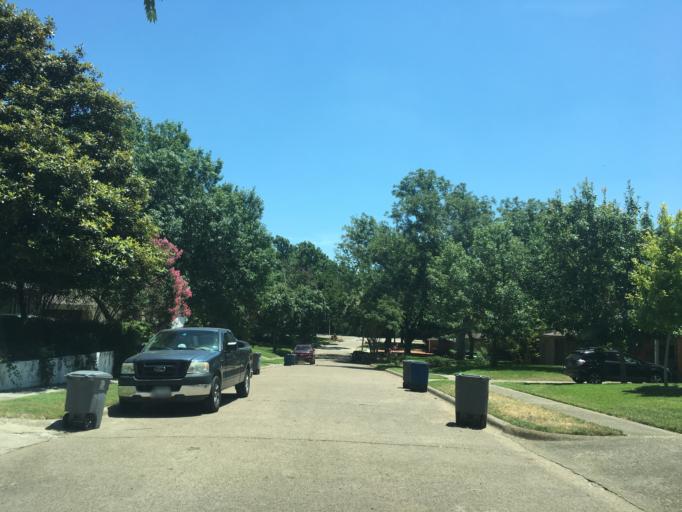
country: US
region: Texas
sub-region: Dallas County
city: Highland Park
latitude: 32.8475
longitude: -96.7055
